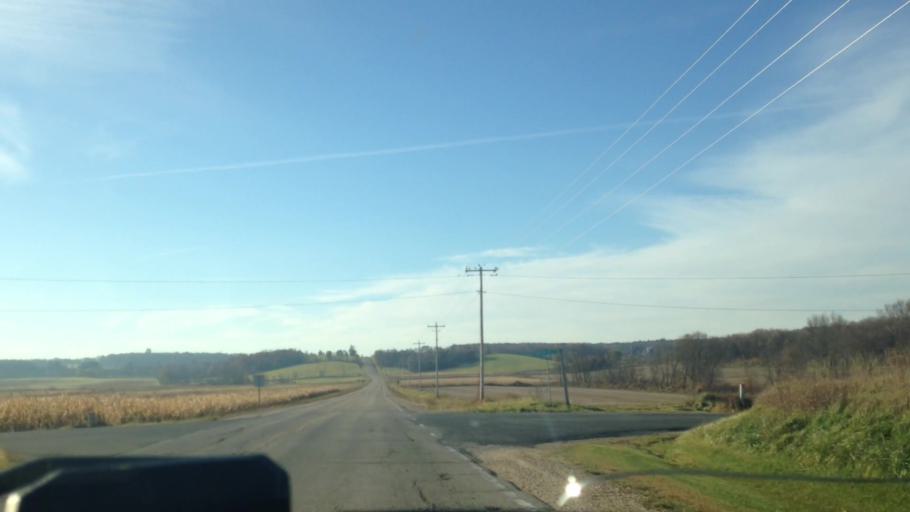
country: US
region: Wisconsin
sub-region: Dodge County
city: Mayville
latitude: 43.4715
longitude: -88.5006
